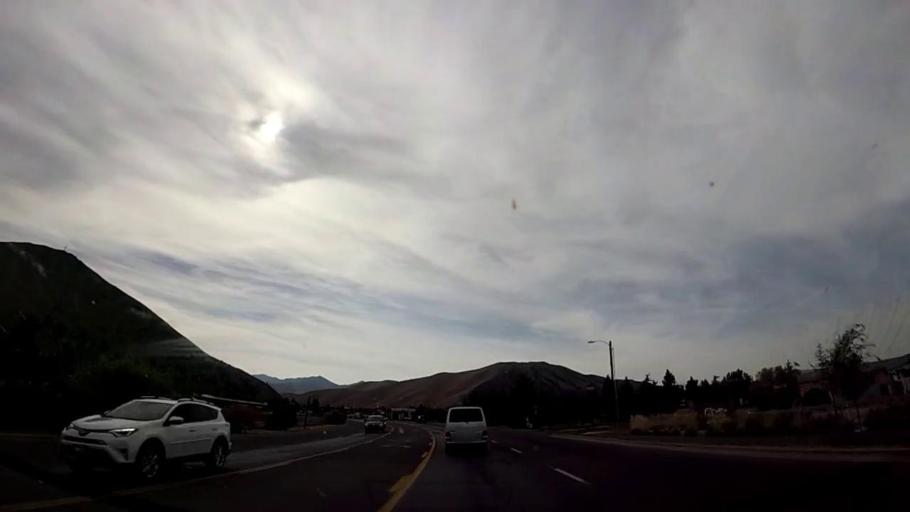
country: US
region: Idaho
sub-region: Blaine County
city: Hailey
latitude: 43.5132
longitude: -114.3038
